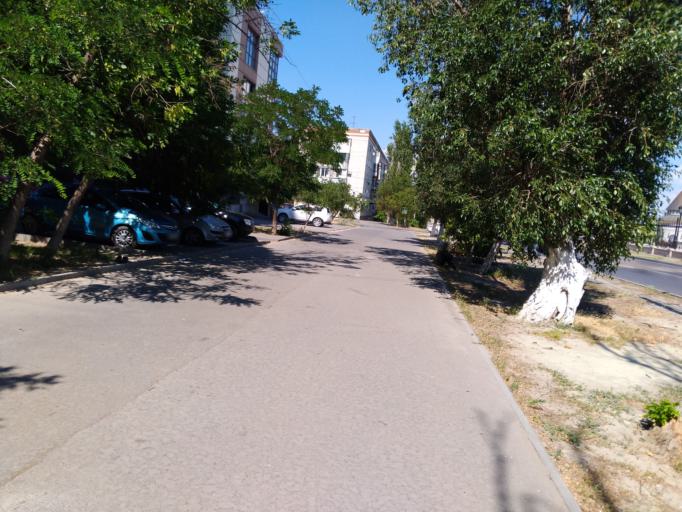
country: RU
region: Volgograd
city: Volgograd
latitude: 48.7189
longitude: 44.5204
